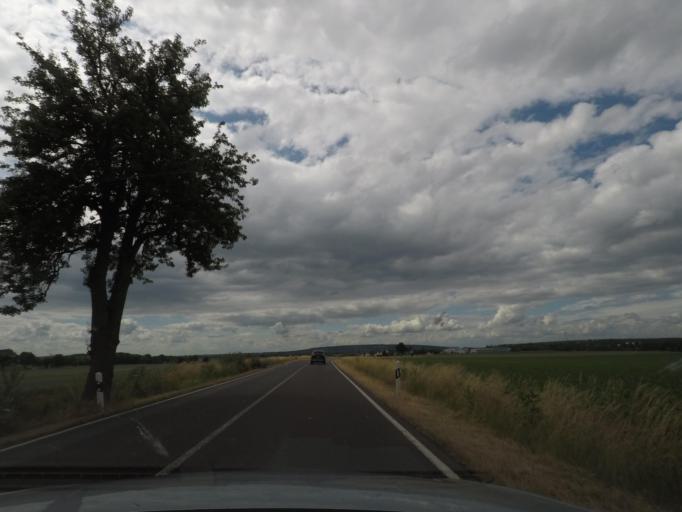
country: DE
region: Saxony-Anhalt
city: Hotensleben
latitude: 52.1067
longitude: 11.0399
